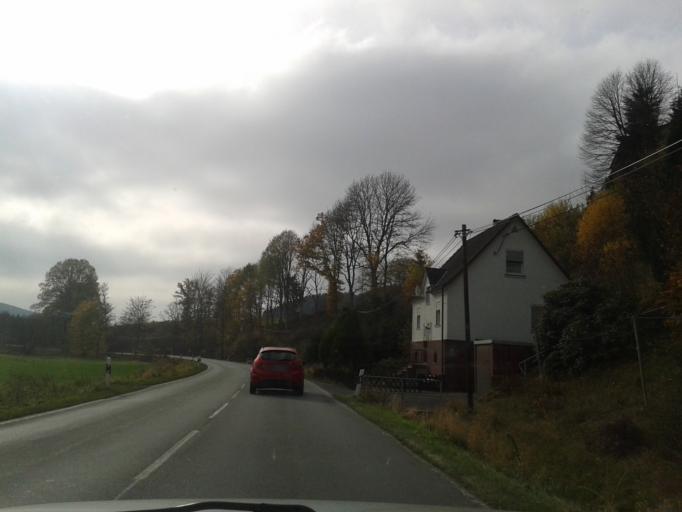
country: DE
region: North Rhine-Westphalia
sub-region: Regierungsbezirk Arnsberg
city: Bad Berleburg
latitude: 51.0812
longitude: 8.4178
